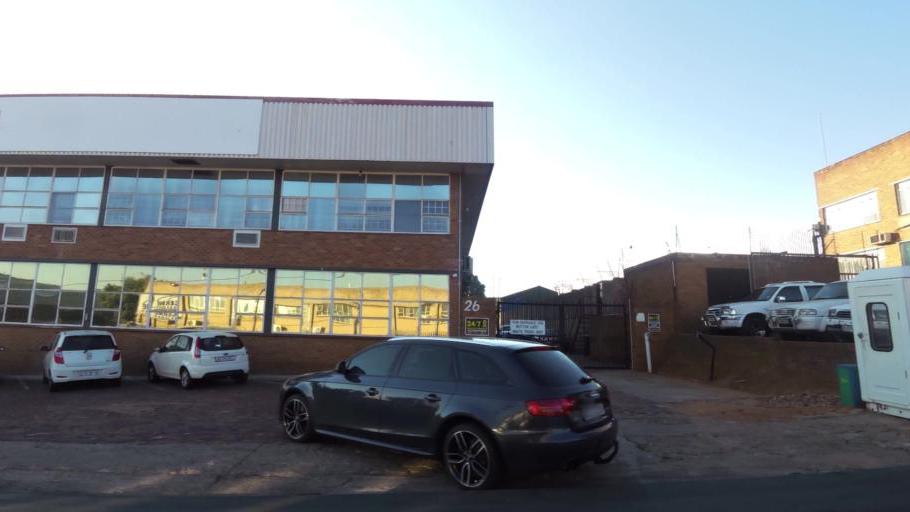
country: ZA
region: Gauteng
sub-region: City of Johannesburg Metropolitan Municipality
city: Modderfontein
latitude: -26.1079
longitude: 28.0798
